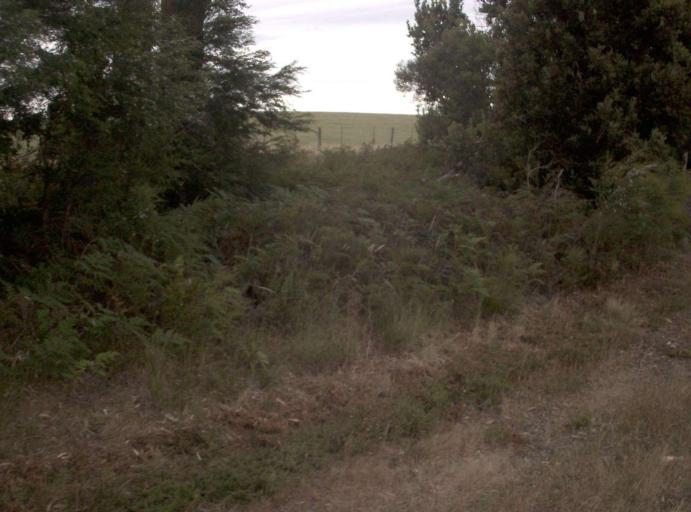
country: AU
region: Victoria
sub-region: Wellington
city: Sale
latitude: -38.0058
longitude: 147.2799
